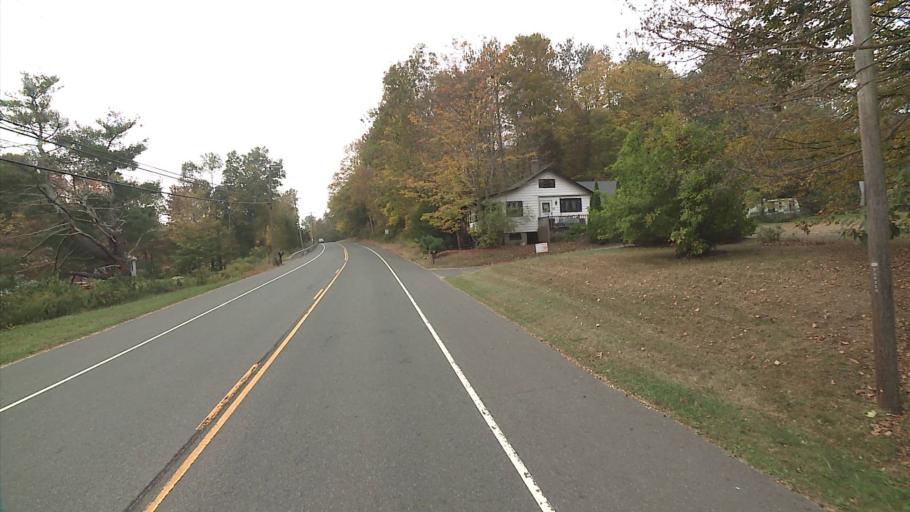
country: US
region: Connecticut
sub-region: Litchfield County
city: Woodbury Center
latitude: 41.5826
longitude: -73.1743
